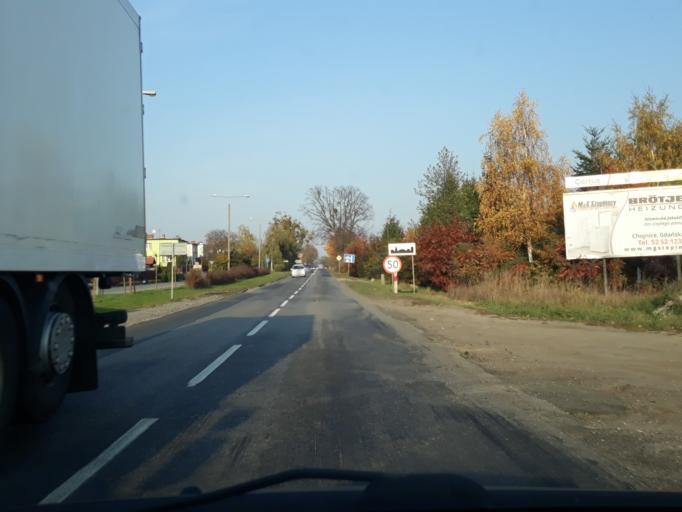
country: PL
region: Pomeranian Voivodeship
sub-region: Powiat chojnicki
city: Chojnice
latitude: 53.6847
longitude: 17.5449
